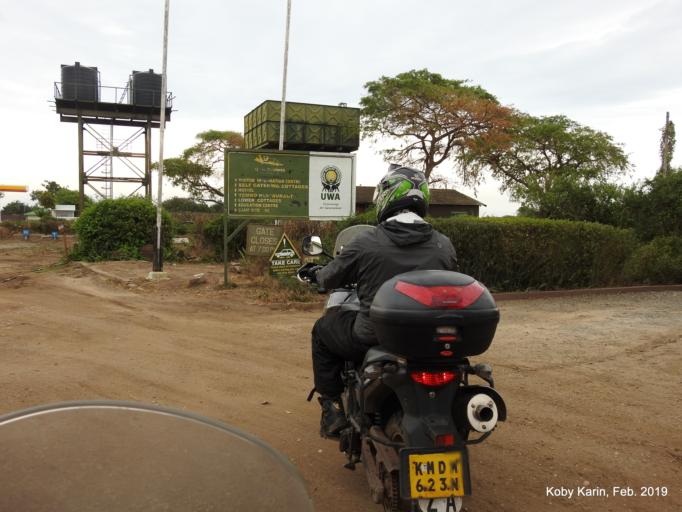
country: UG
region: Western Region
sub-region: Rubirizi District
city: Rubirizi
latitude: -0.1894
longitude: 29.8990
